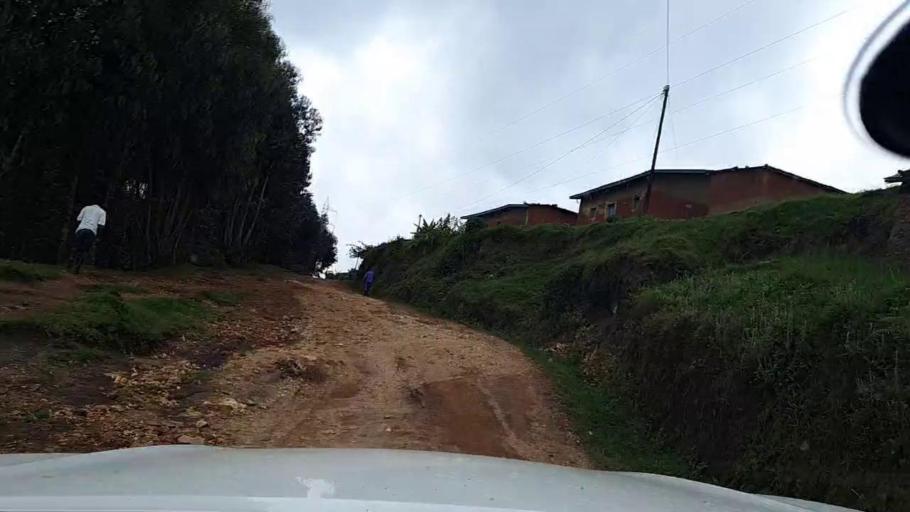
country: RW
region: Western Province
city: Kibuye
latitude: -2.1763
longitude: 29.4467
